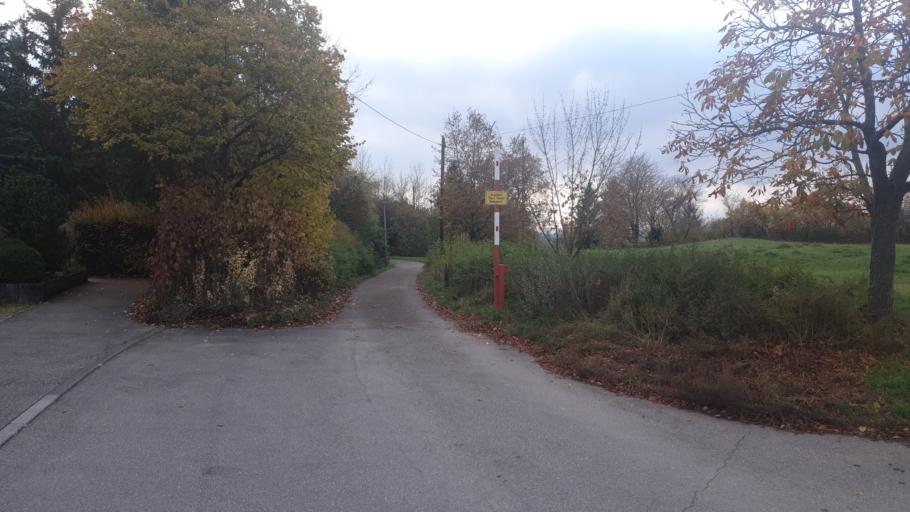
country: DE
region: Baden-Wuerttemberg
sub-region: Regierungsbezirk Stuttgart
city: Leonberg
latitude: 48.7919
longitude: 9.0278
